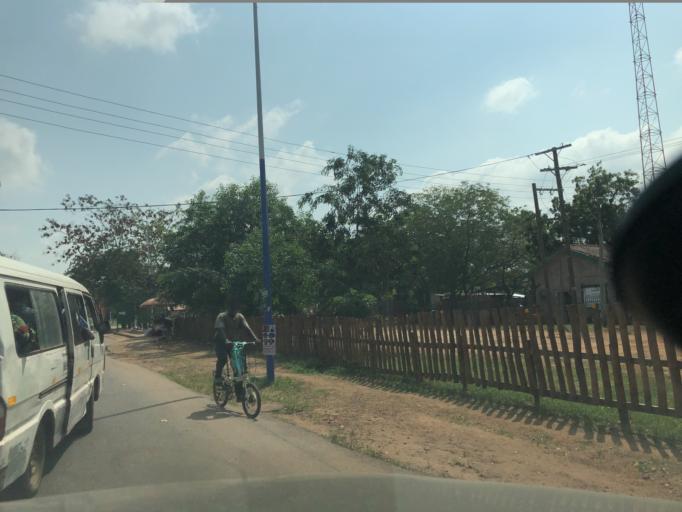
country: GH
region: Greater Accra
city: Medina Estates
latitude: 5.6673
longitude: -0.1877
